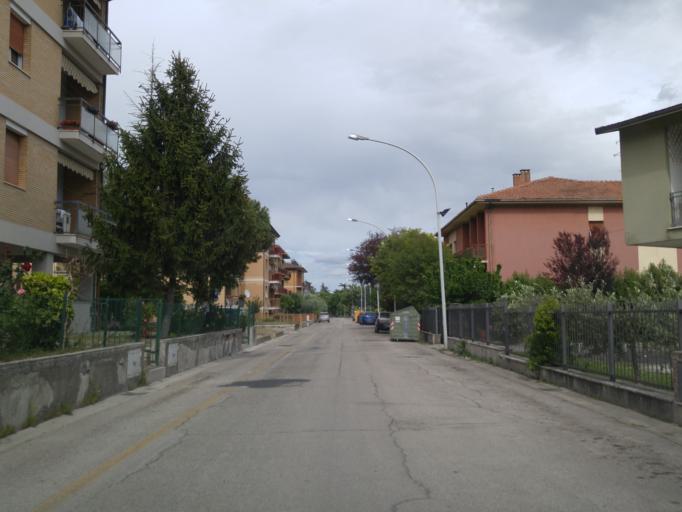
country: IT
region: The Marches
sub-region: Provincia di Pesaro e Urbino
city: Fossombrone
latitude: 43.6932
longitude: 12.8161
